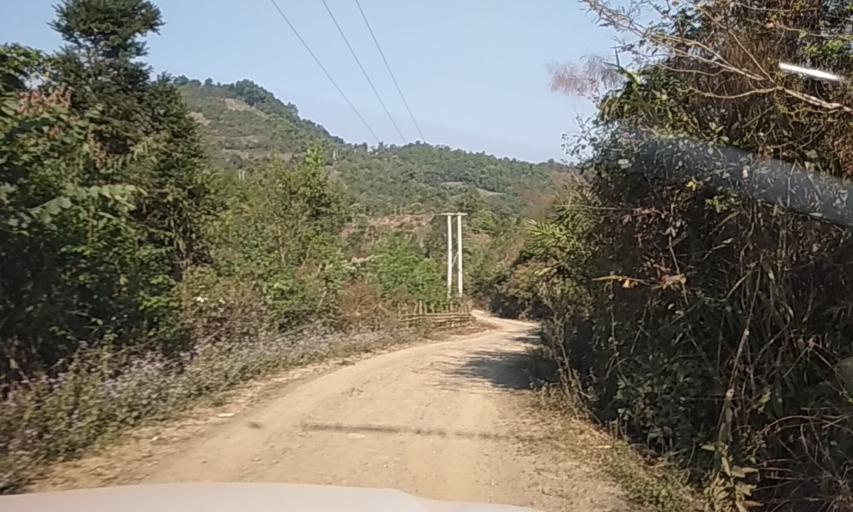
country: LA
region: Phongsali
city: Phongsali
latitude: 21.6935
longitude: 102.0888
